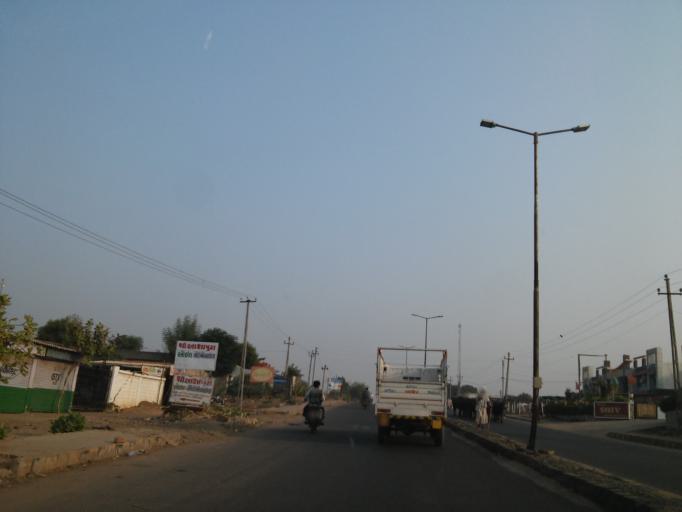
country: IN
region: Gujarat
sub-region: Kachchh
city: Bhachau
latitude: 23.2956
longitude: 70.3486
